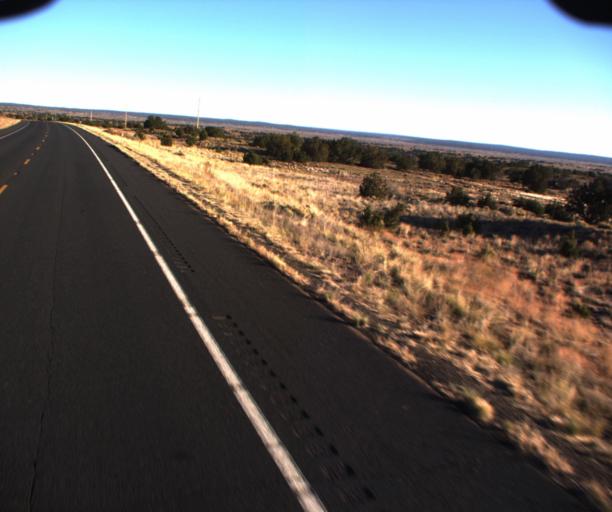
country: US
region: Arizona
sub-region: Apache County
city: Houck
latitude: 35.2595
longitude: -109.4379
